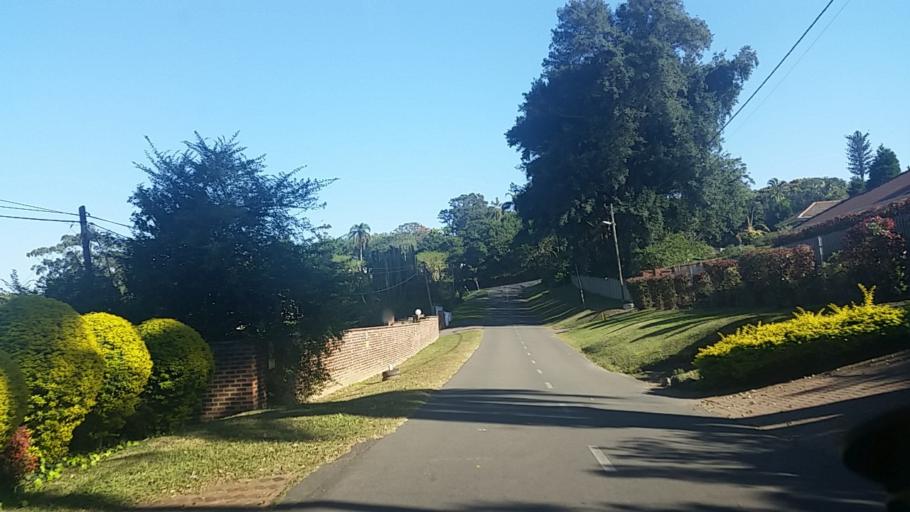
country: ZA
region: KwaZulu-Natal
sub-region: eThekwini Metropolitan Municipality
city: Berea
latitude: -29.8415
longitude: 30.9022
